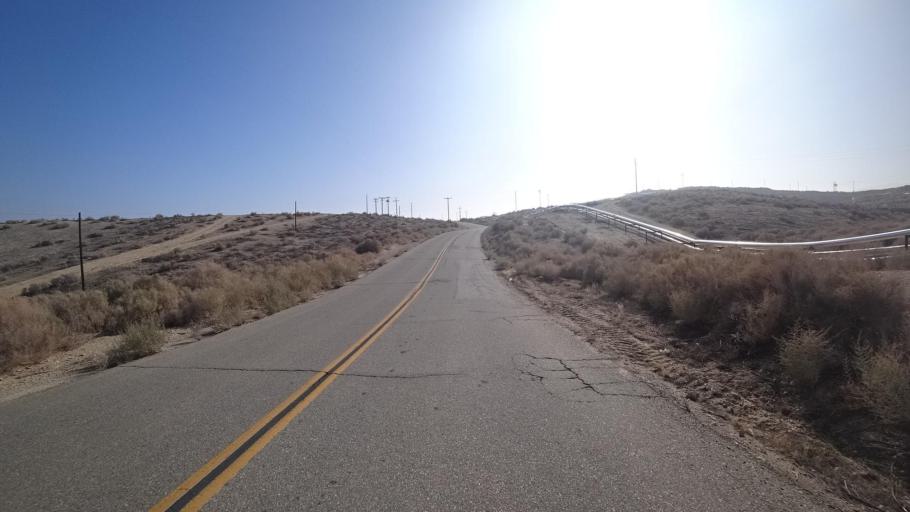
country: US
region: California
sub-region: Kern County
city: Taft Heights
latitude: 35.1459
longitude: -119.5136
